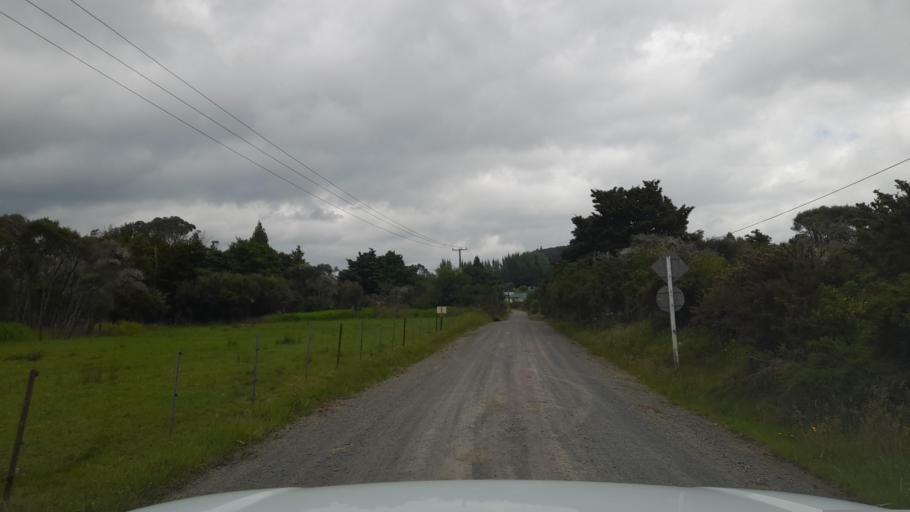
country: NZ
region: Northland
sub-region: Far North District
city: Waimate North
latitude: -35.3996
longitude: 173.7860
